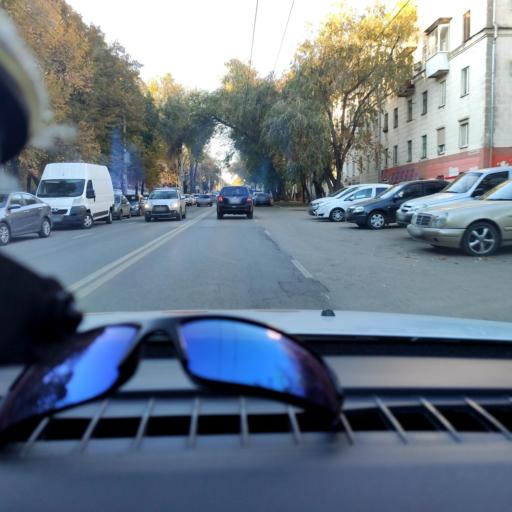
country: RU
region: Samara
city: Samara
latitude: 53.2122
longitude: 50.2418
